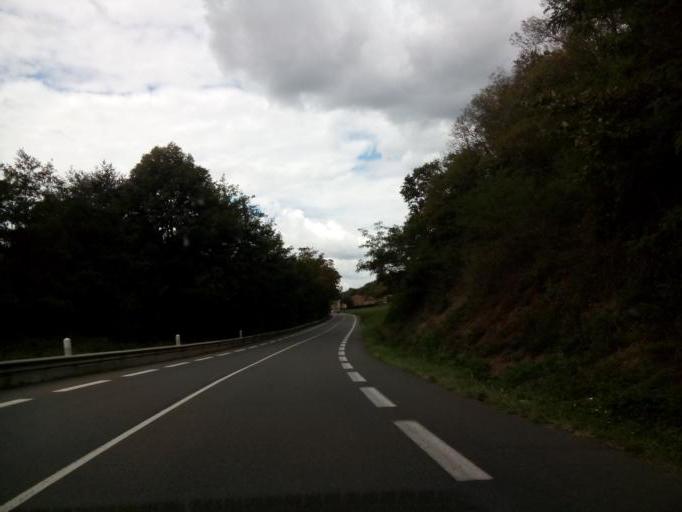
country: FR
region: Rhone-Alpes
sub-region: Departement du Rhone
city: Chatillon
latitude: 45.8915
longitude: 4.6004
